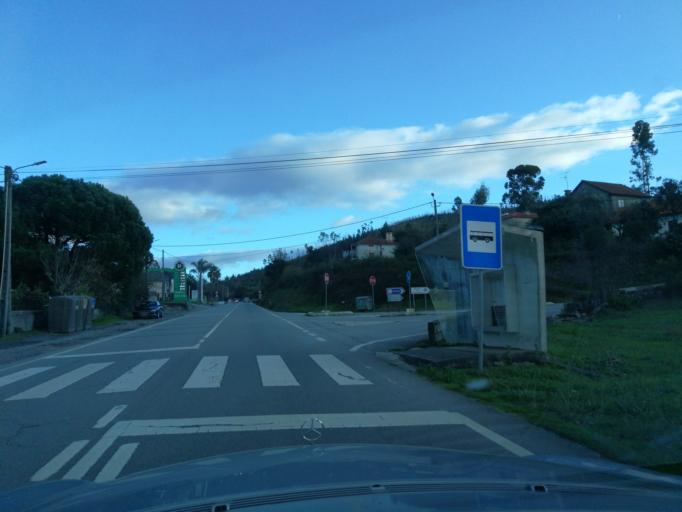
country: PT
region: Braga
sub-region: Barcelos
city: Vila Frescainha
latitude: 41.5711
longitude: -8.6868
